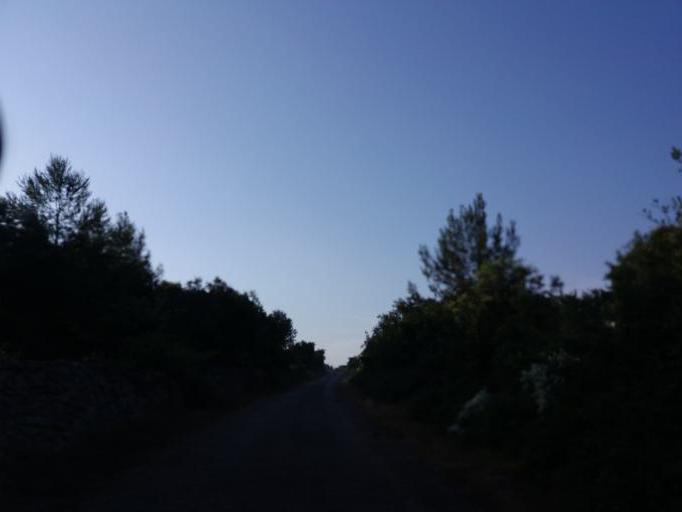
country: HR
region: Zadarska
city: Sali
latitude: 43.9131
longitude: 15.1339
